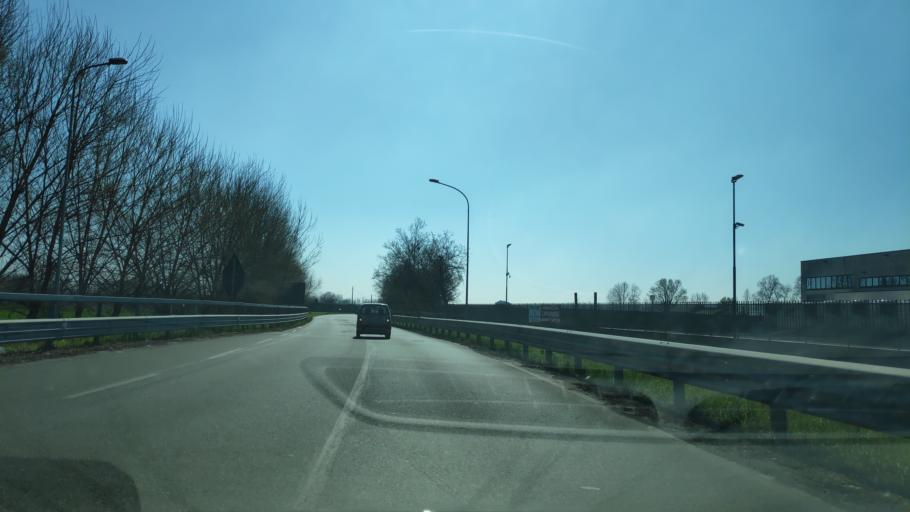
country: IT
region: Lombardy
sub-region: Citta metropolitana di Milano
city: Premenugo
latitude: 45.4818
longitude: 9.3800
